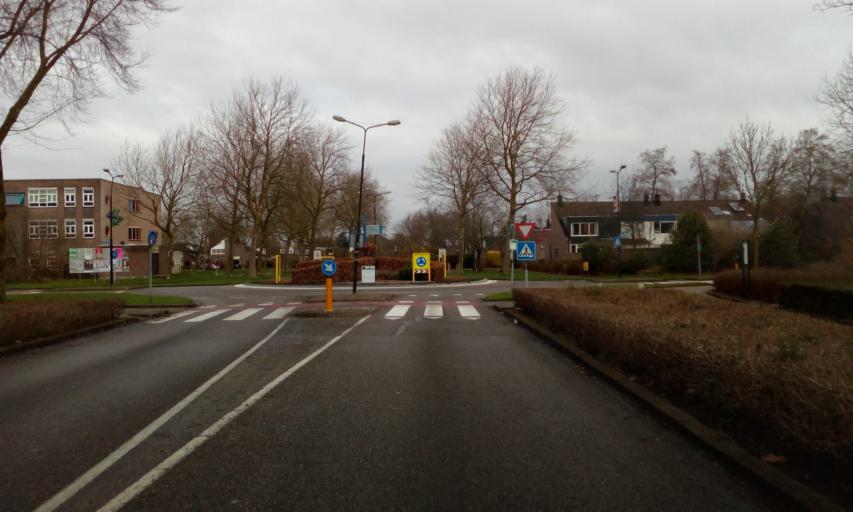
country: NL
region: Utrecht
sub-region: Gemeente De Ronde Venen
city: Mijdrecht
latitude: 52.2136
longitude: 4.8619
